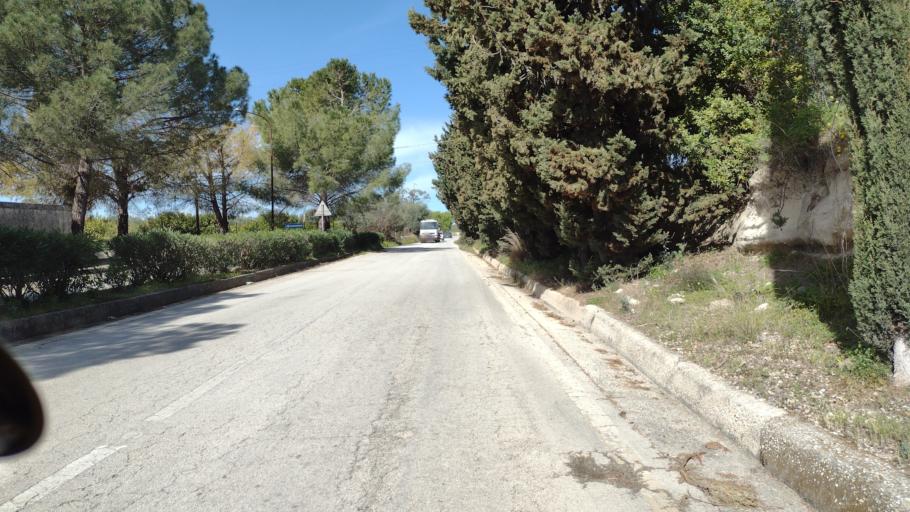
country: IT
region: Sicily
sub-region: Provincia di Siracusa
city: Noto
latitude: 36.8861
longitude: 15.0567
